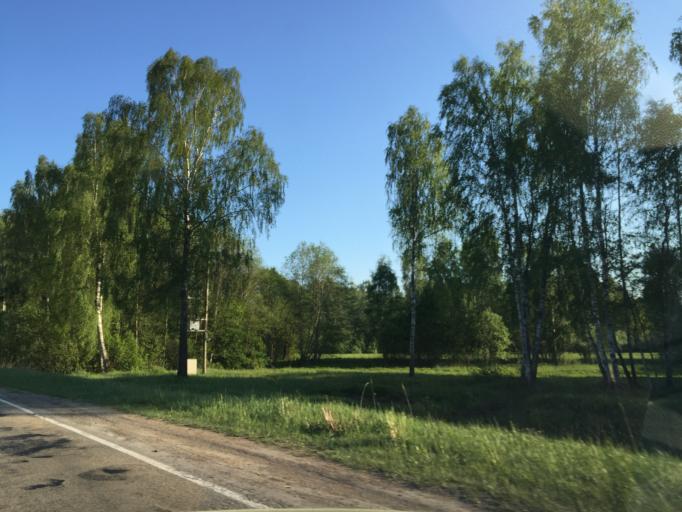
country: LV
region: Kekava
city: Kekava
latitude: 56.7823
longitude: 24.2986
